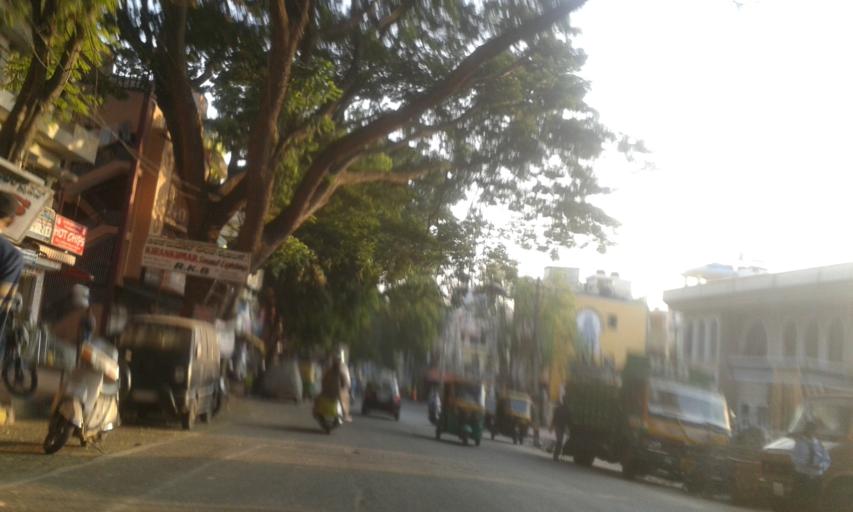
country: IN
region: Karnataka
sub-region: Bangalore Urban
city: Bangalore
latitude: 12.9197
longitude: 77.5896
